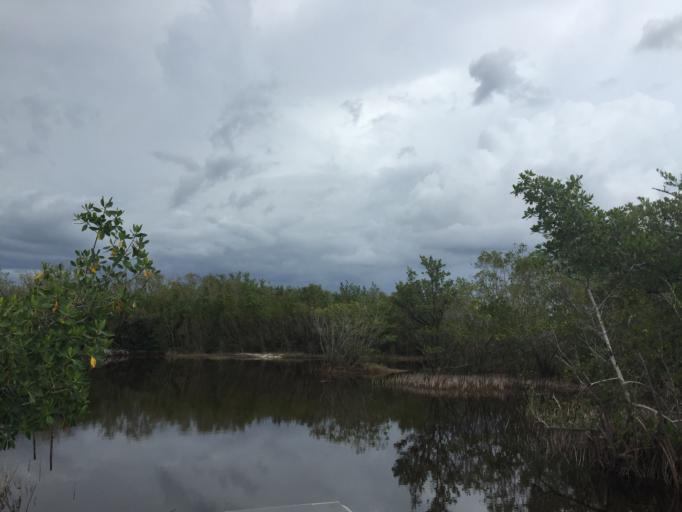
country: US
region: Florida
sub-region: Collier County
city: Marco
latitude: 25.9081
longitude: -81.3677
